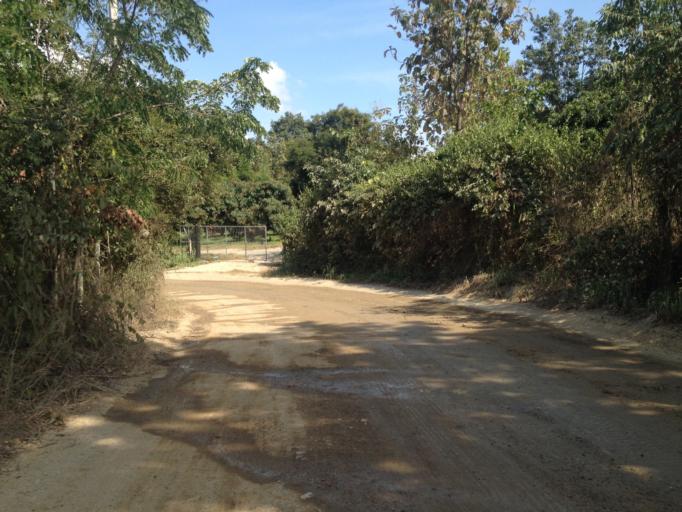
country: TH
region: Chiang Mai
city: Hang Dong
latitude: 18.6957
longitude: 98.8726
